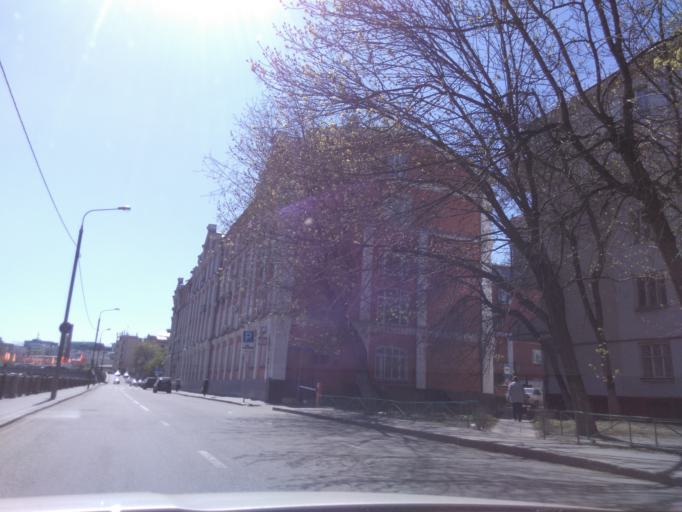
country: RU
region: Moscow
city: Zamoskvorech'ye
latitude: 55.7356
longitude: 37.6401
